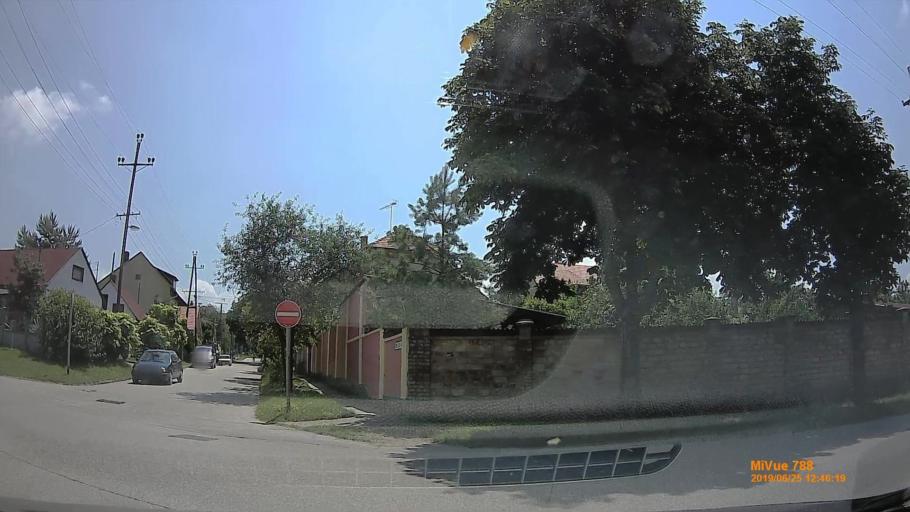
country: HU
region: Komarom-Esztergom
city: Esztergom
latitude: 47.8043
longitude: 18.7472
